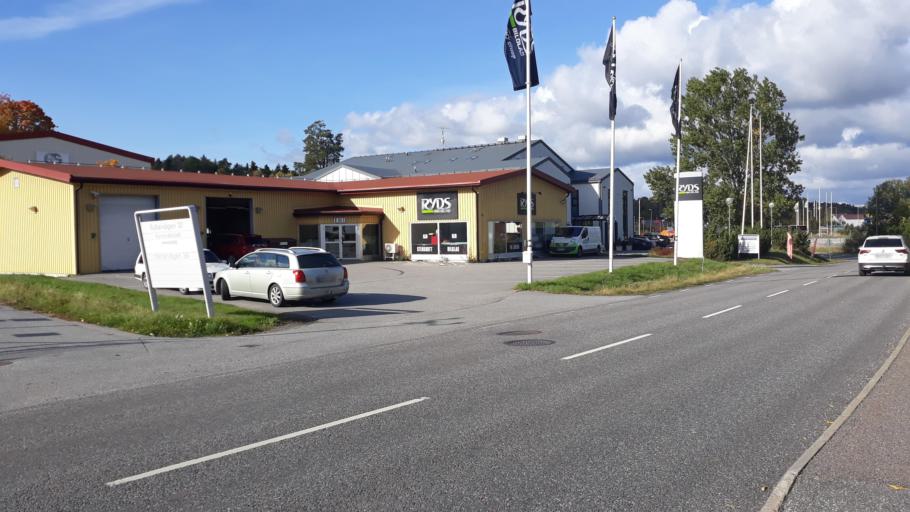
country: SE
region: Stockholm
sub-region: Osterakers Kommun
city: Akersberga
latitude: 59.4845
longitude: 18.2777
